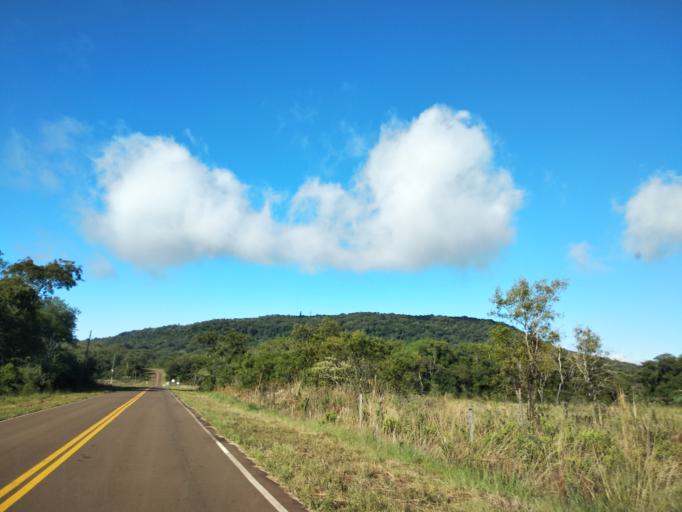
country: AR
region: Misiones
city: Santa Ana
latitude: -27.4308
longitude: -55.5734
